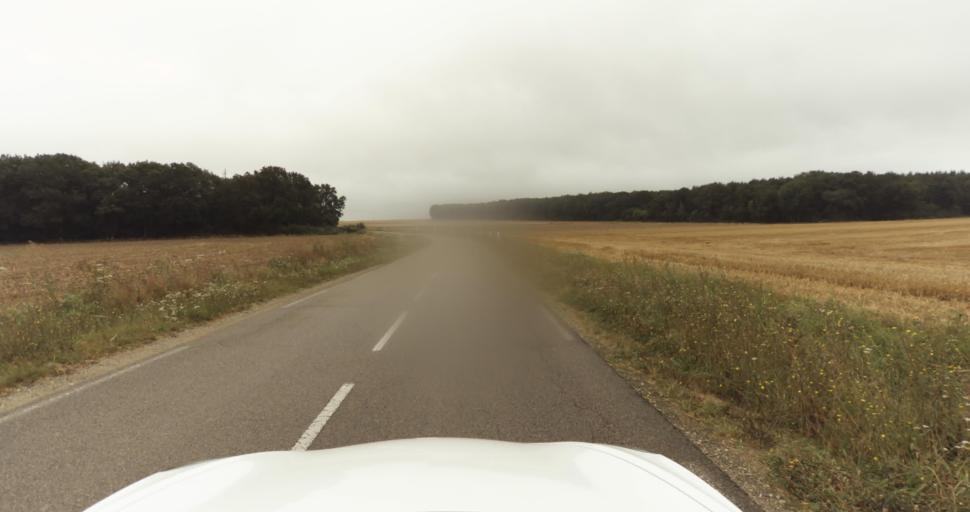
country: FR
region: Haute-Normandie
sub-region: Departement de l'Eure
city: Normanville
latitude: 49.0930
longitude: 1.1688
